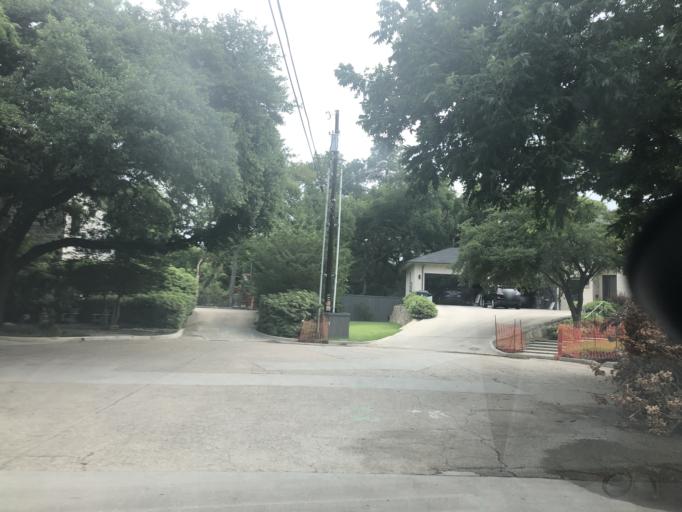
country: US
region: Texas
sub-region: Dallas County
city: University Park
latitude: 32.8593
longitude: -96.8434
